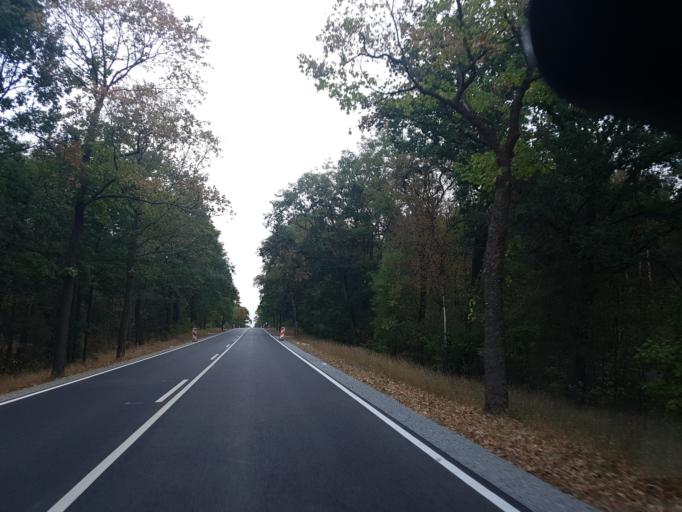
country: DE
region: Brandenburg
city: Treuenbrietzen
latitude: 52.0506
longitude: 12.8171
